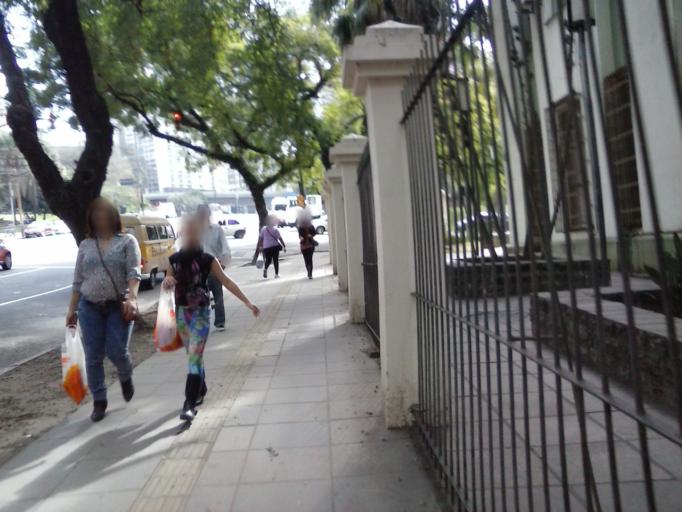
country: BR
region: Rio Grande do Sul
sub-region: Porto Alegre
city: Porto Alegre
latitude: -30.0331
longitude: -51.2225
